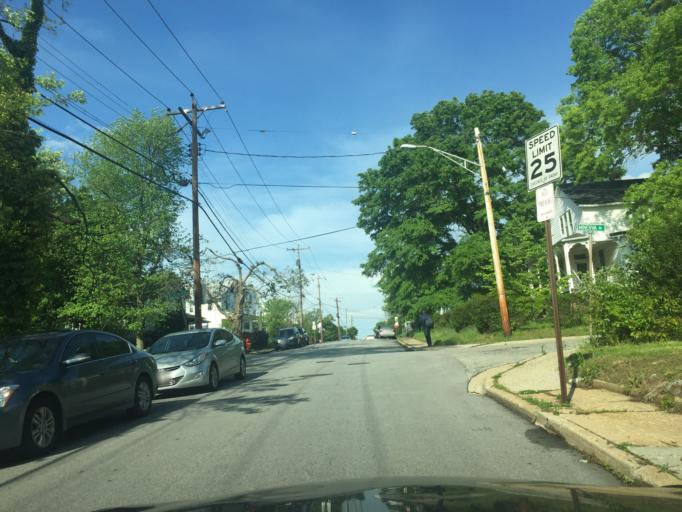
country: US
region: Maryland
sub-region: City of Baltimore
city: Baltimore
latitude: 39.3433
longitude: -76.6013
